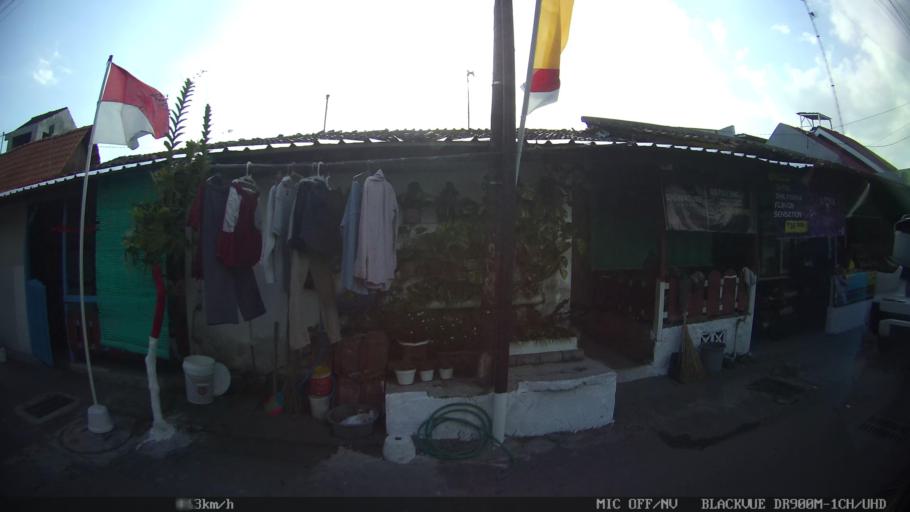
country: ID
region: Daerah Istimewa Yogyakarta
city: Yogyakarta
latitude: -7.7910
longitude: 110.3507
